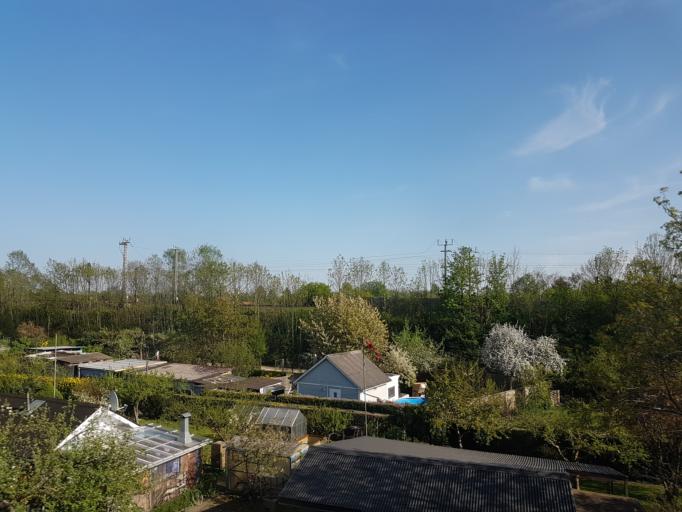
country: DE
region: Lower Saxony
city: Laatzen
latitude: 52.3462
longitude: 9.7710
